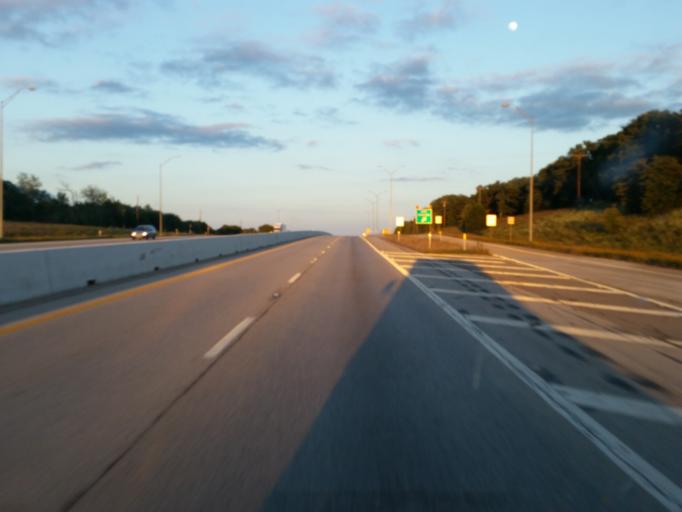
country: US
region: Texas
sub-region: Van Zandt County
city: Van
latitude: 32.4937
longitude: -95.5627
